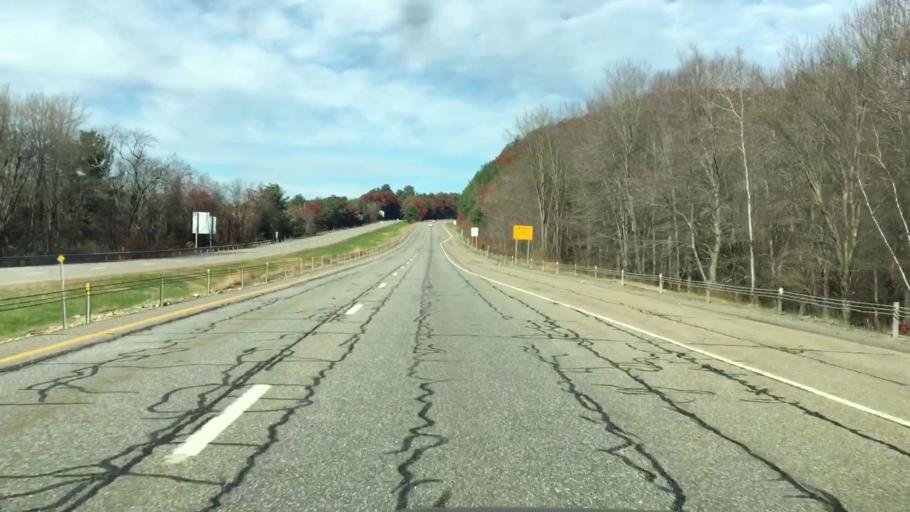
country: US
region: Connecticut
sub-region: Litchfield County
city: Torrington
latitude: 41.7663
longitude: -73.1150
